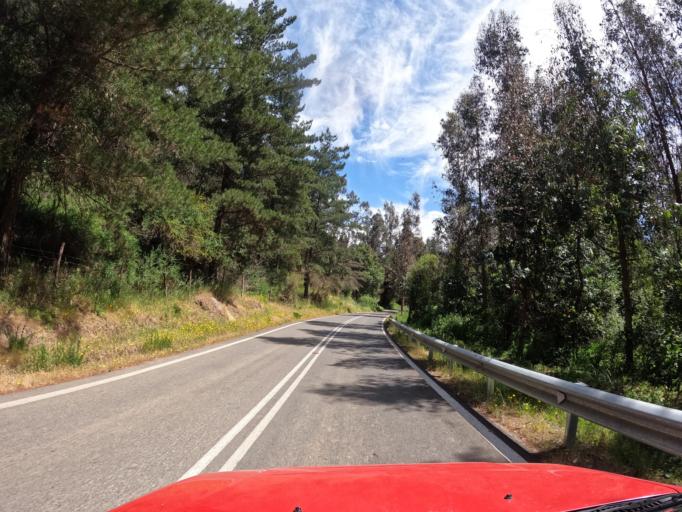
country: CL
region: Maule
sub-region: Provincia de Talca
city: Talca
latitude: -34.9947
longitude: -71.8782
